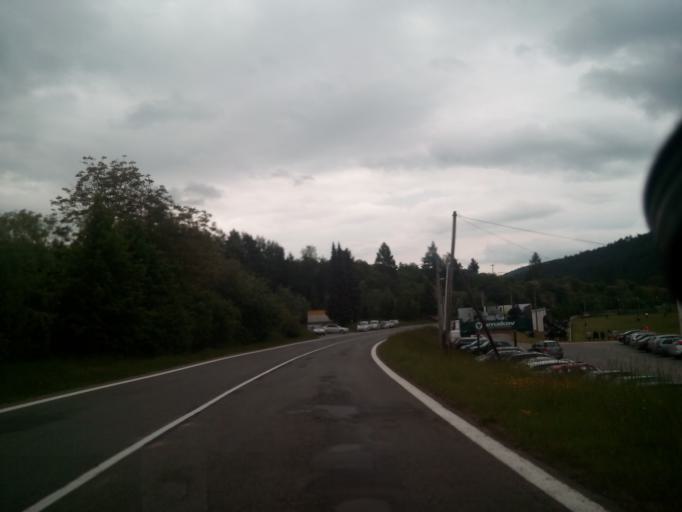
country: SK
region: Kosicky
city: Krompachy
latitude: 49.0137
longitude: 20.9472
